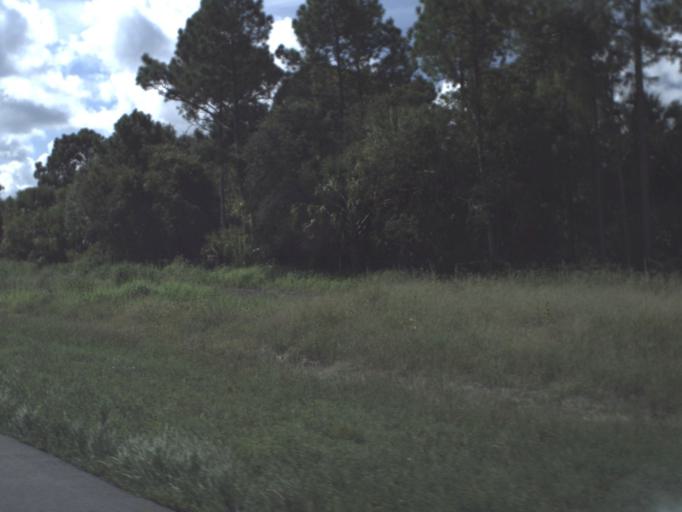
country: US
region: Florida
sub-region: Charlotte County
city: Port Charlotte
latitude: 27.0639
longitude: -82.0897
